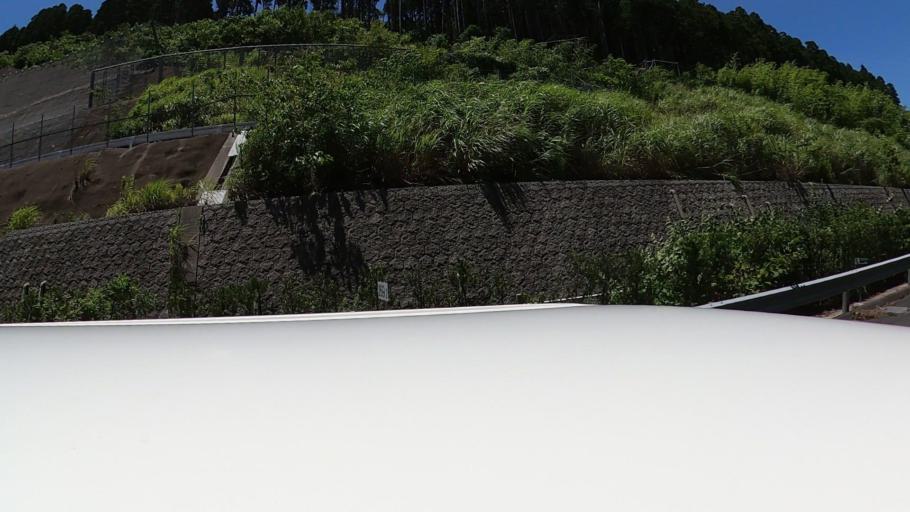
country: JP
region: Miyazaki
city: Nobeoka
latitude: 32.3933
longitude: 131.6216
